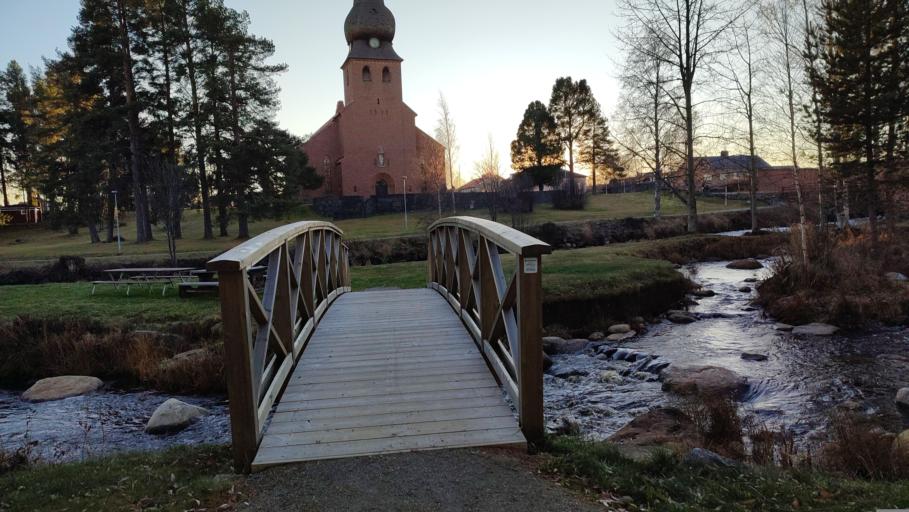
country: SE
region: Vaesterbotten
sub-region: Skelleftea Kommun
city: Burea
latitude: 64.6192
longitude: 21.2042
